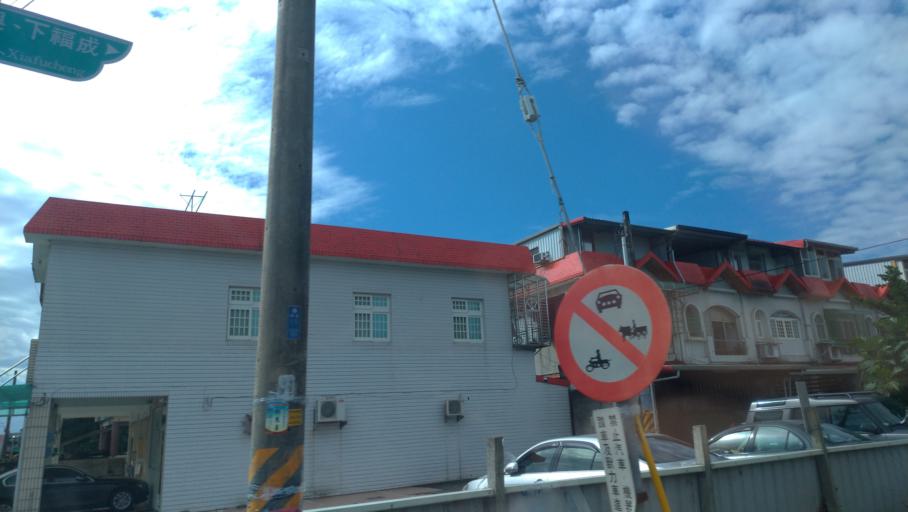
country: TW
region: Taiwan
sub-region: Yilan
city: Yilan
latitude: 24.8525
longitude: 121.8183
